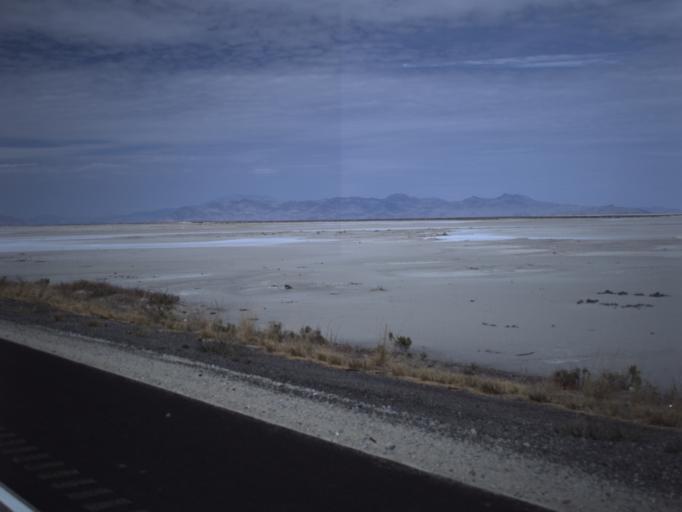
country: US
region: Utah
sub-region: Tooele County
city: Wendover
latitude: 40.7312
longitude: -113.4741
